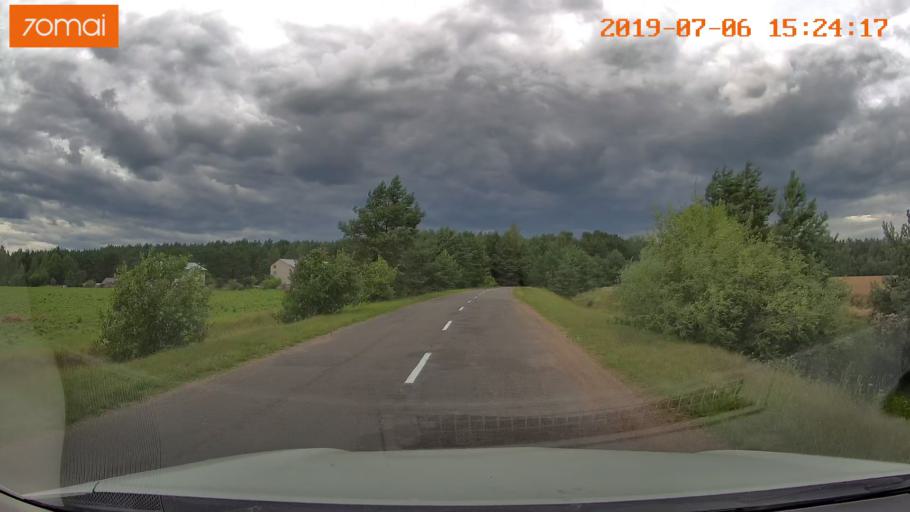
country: BY
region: Minsk
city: Valozhyn
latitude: 54.0185
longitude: 26.6030
